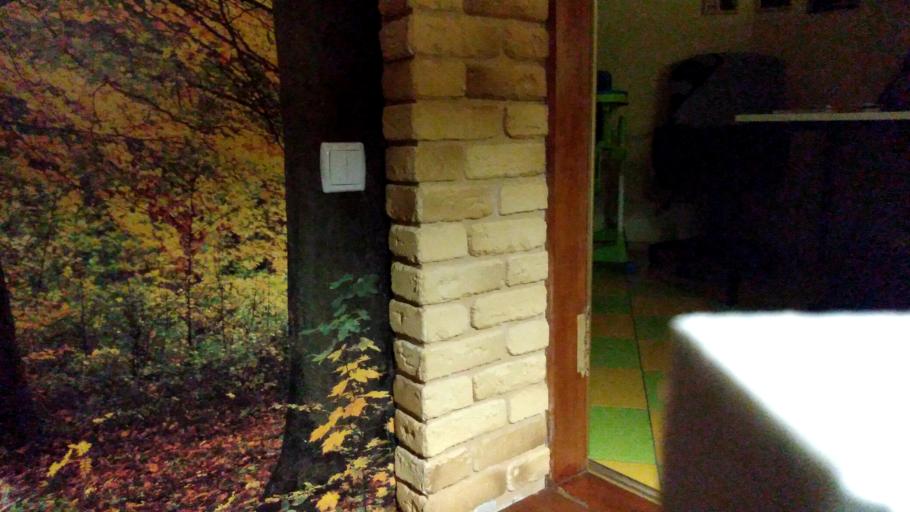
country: RU
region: Arkhangelskaya
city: Kargopol'
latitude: 61.4078
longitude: 37.8135
